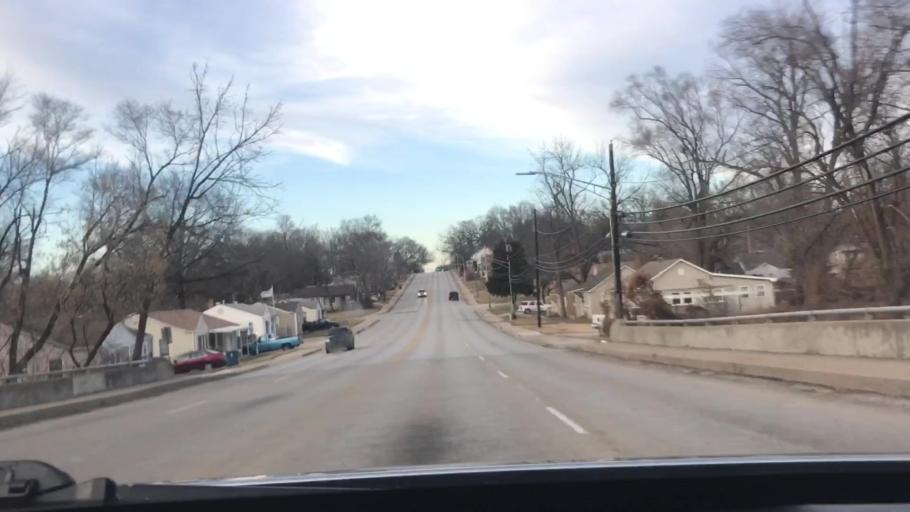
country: US
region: Missouri
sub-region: Jackson County
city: Independence
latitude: 39.0742
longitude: -94.4463
